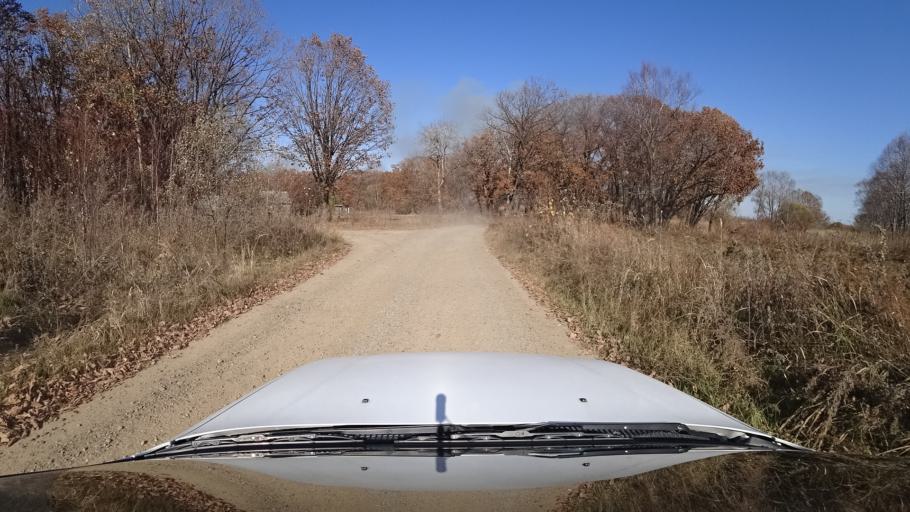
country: RU
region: Primorskiy
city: Dal'nerechensk
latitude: 45.8823
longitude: 133.7351
